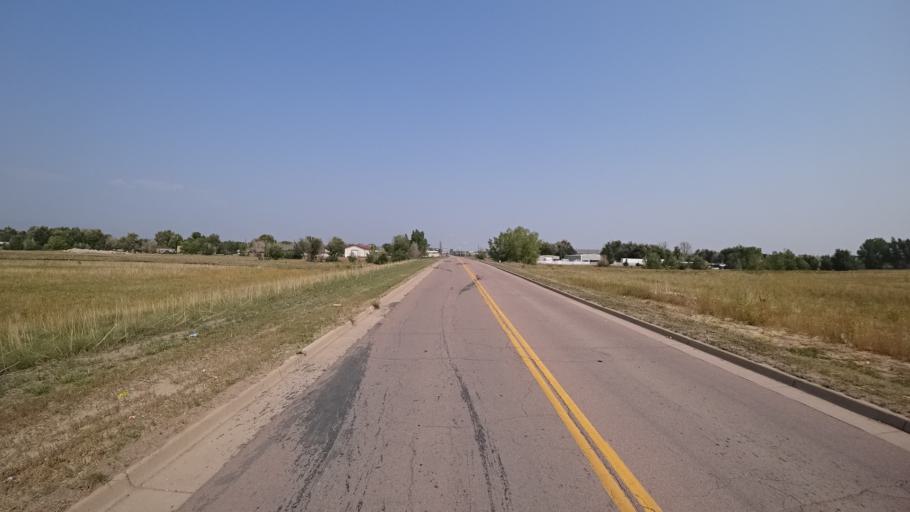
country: US
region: Colorado
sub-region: El Paso County
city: Cimarron Hills
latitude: 38.8287
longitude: -104.7250
